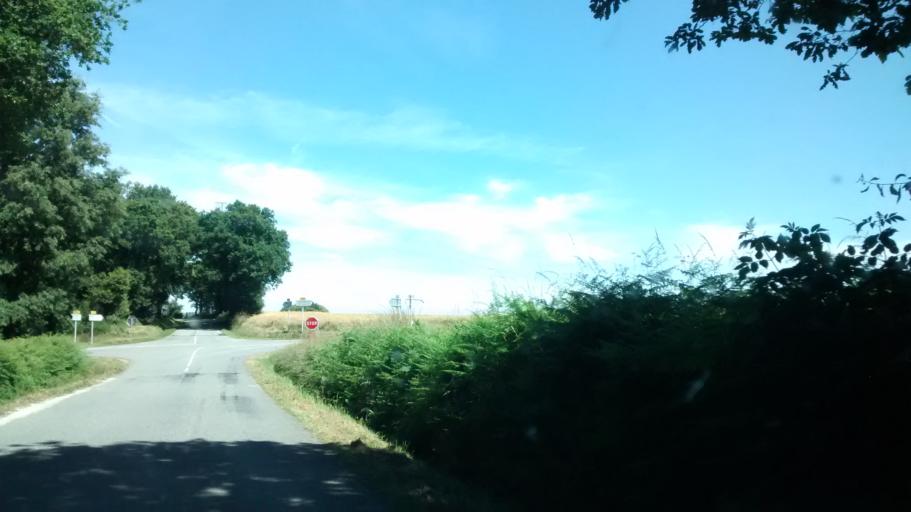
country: FR
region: Brittany
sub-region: Departement du Morbihan
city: Campeneac
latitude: 47.9926
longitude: -2.3065
